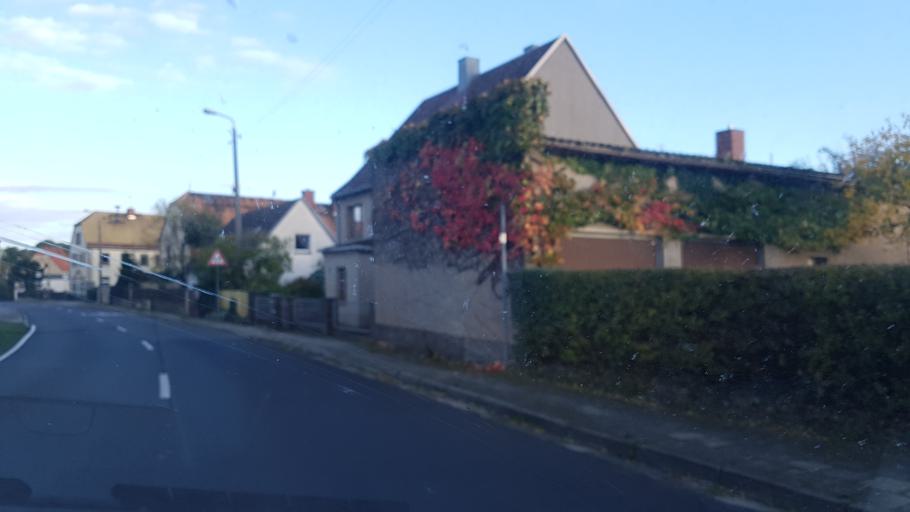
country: DE
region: Saxony
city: Dahlen
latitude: 51.3378
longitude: 13.0301
